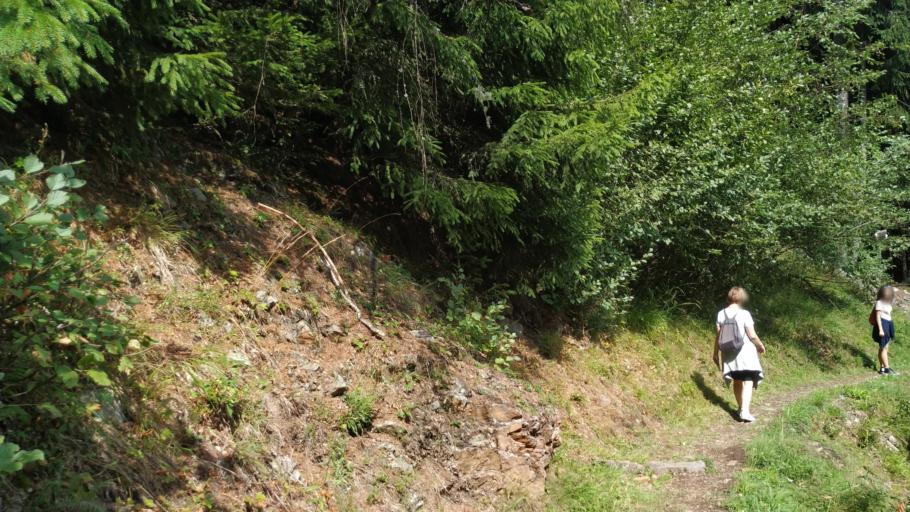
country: IT
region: Trentino-Alto Adige
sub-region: Bolzano
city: Rabla
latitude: 46.6883
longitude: 11.0468
